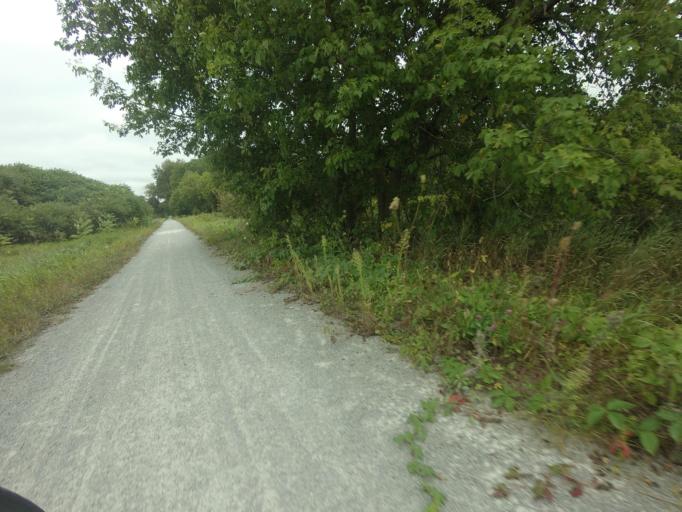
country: CA
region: Ontario
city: Omemee
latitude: 44.3302
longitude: -78.7701
